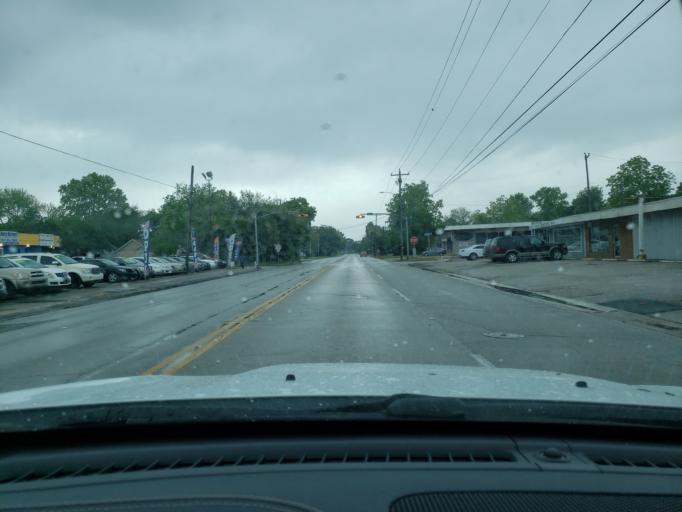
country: US
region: Texas
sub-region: Harris County
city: Baytown
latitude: 29.7446
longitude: -94.9722
